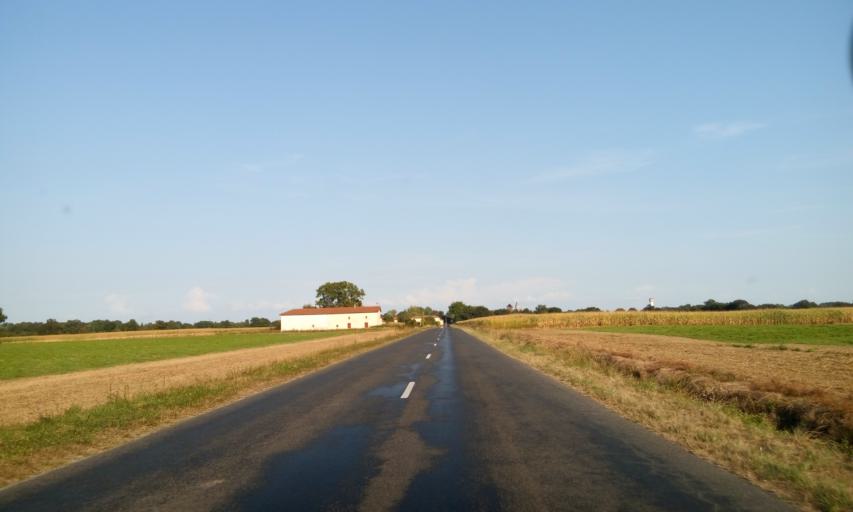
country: FR
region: Rhone-Alpes
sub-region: Departement de l'Ain
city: Amberieux-en-Dombes
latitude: 46.0006
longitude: 4.8843
